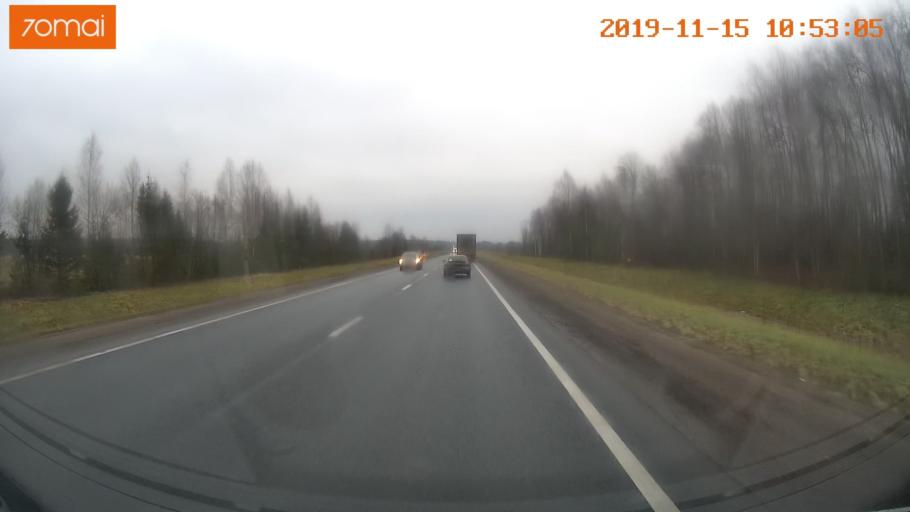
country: RU
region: Vologda
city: Chebsara
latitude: 59.1709
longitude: 38.7469
